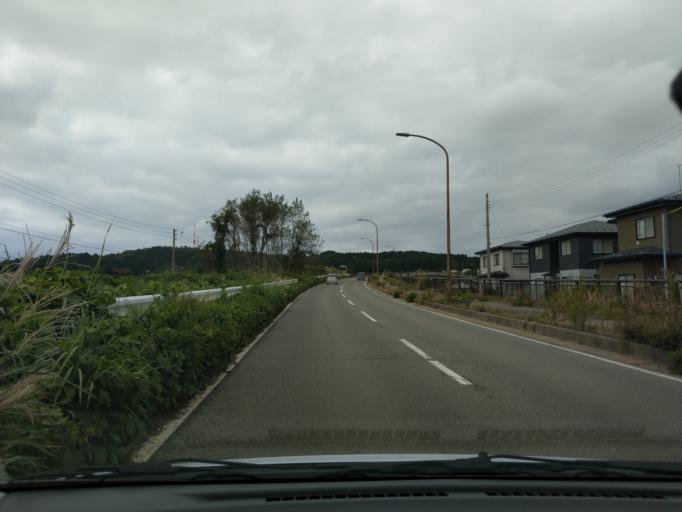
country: JP
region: Akita
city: Akita Shi
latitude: 39.6689
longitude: 140.0905
